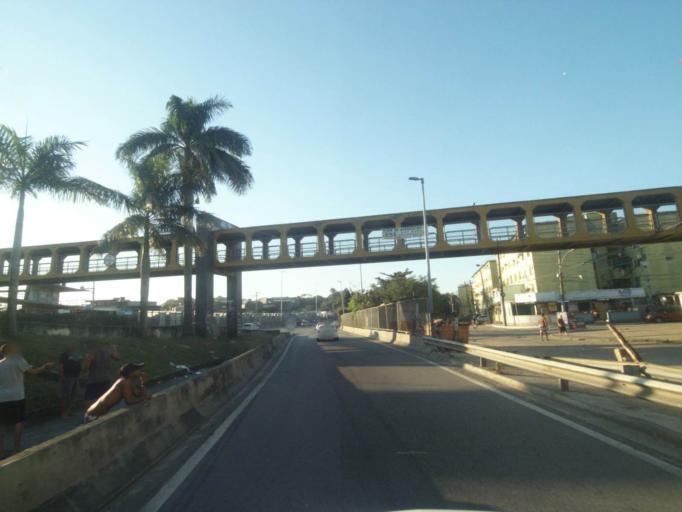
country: BR
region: Rio de Janeiro
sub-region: Sao Joao De Meriti
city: Sao Joao de Meriti
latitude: -22.9519
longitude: -43.3567
